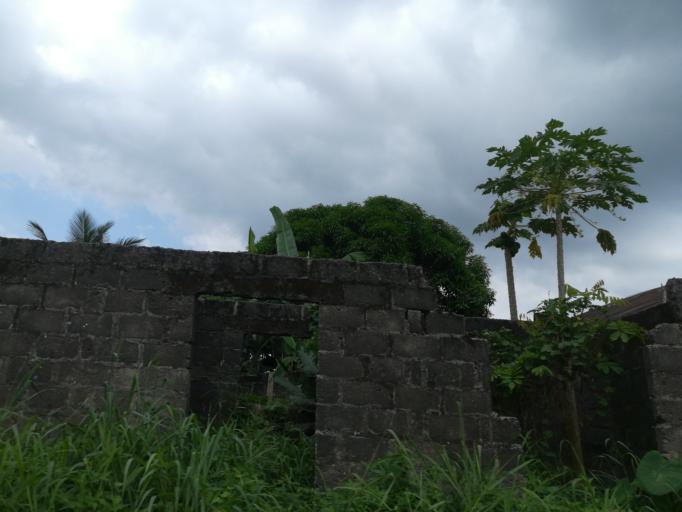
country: NG
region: Rivers
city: Okrika
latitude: 4.7277
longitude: 7.1467
